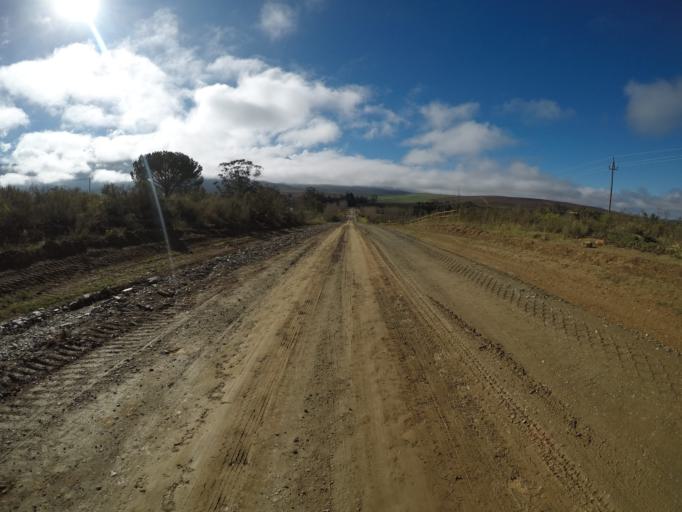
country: ZA
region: Western Cape
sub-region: Overberg District Municipality
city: Caledon
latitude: -34.1138
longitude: 19.7436
